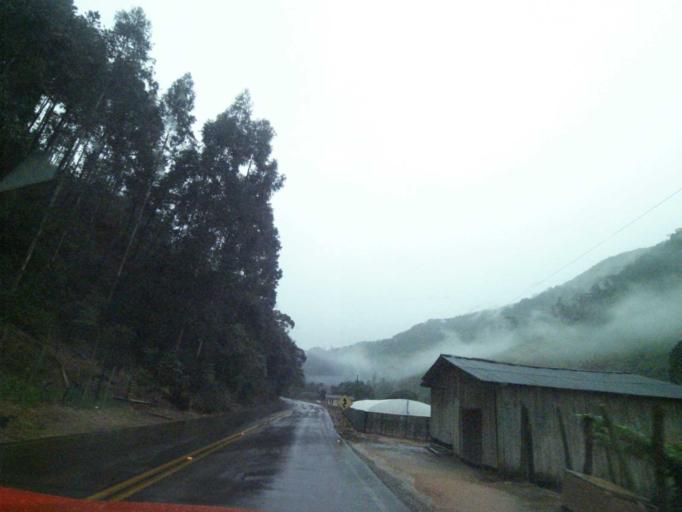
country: BR
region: Santa Catarina
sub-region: Anitapolis
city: Anitapolis
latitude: -27.8314
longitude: -49.0514
